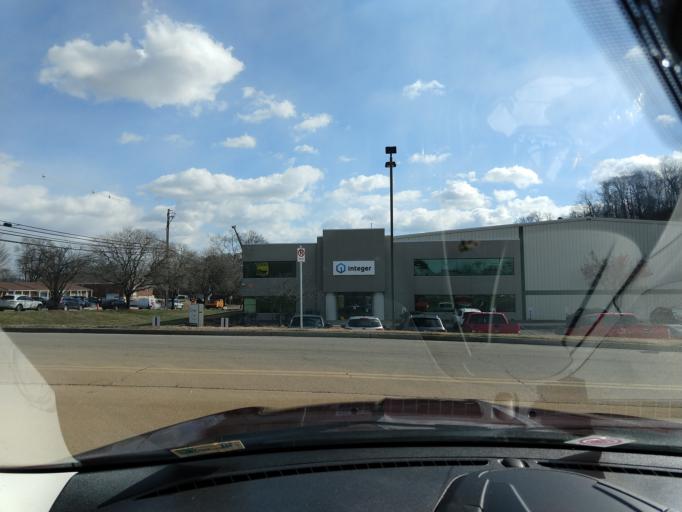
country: US
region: Virginia
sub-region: City of Salem
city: Salem
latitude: 37.2730
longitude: -80.0500
